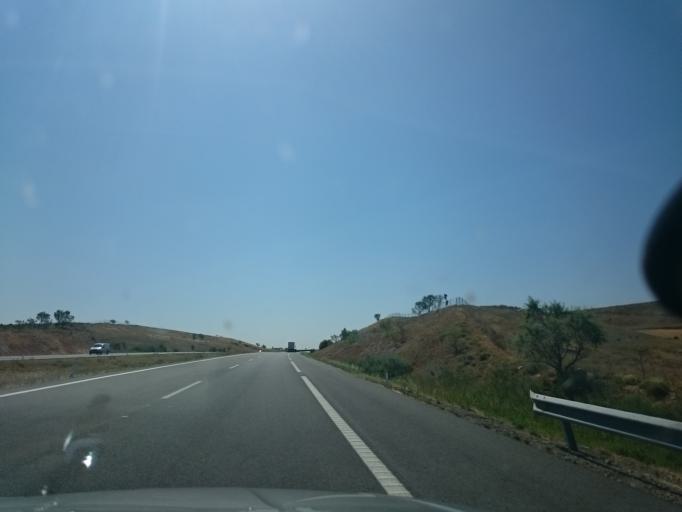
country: ES
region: Navarre
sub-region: Provincia de Navarra
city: Ribaforada
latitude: 41.9764
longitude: -1.5518
